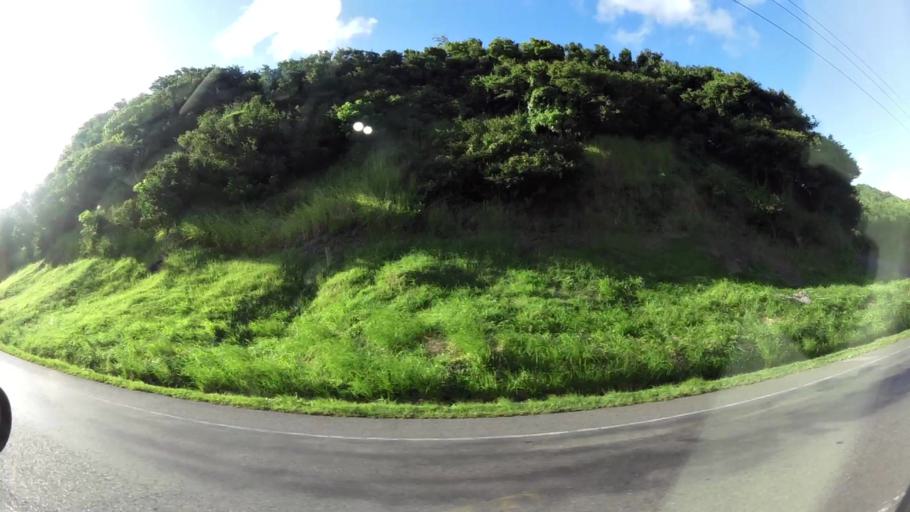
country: TT
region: Tobago
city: Scarborough
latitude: 11.1797
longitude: -60.7049
